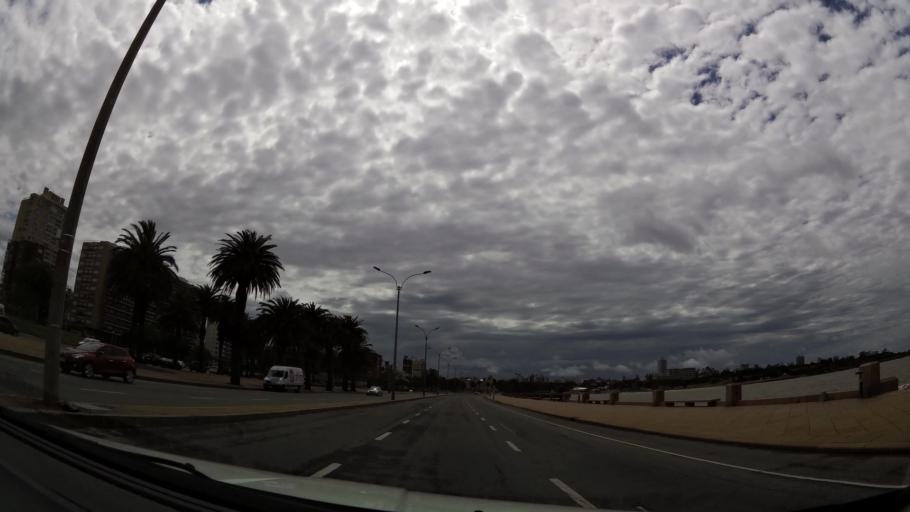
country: UY
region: Montevideo
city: Montevideo
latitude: -34.9146
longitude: -56.1787
